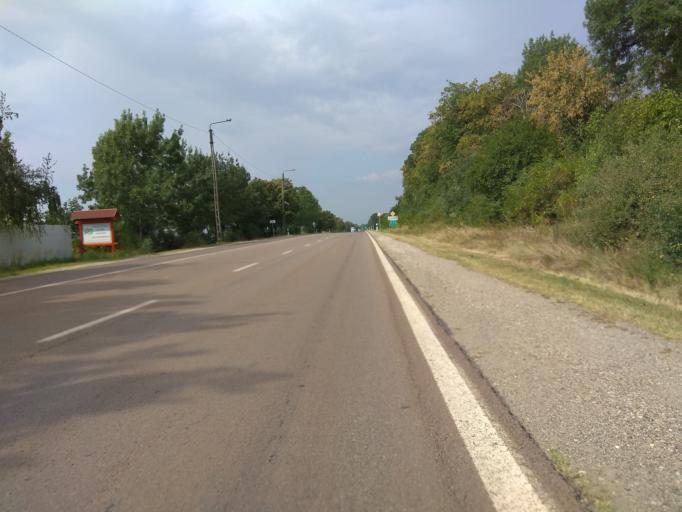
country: HU
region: Borsod-Abauj-Zemplen
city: Emod
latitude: 47.9304
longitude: 20.8031
